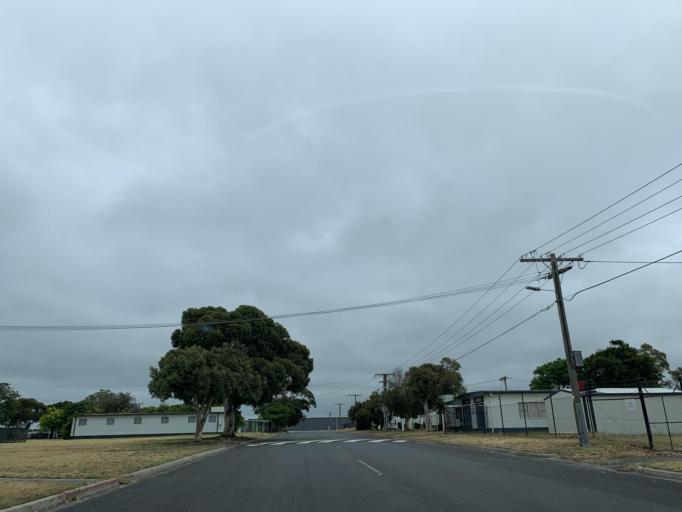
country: AU
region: Victoria
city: Heatherton
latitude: -37.9757
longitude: 145.0919
